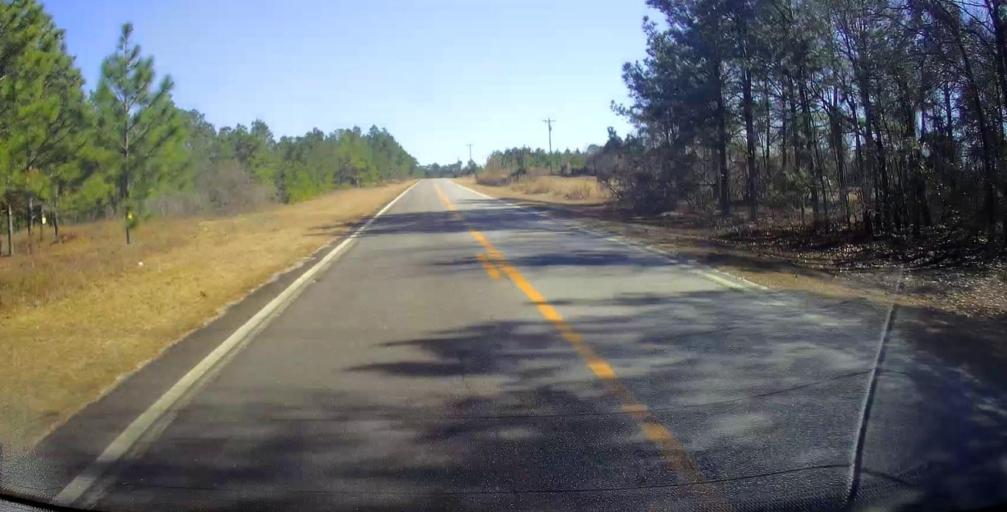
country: US
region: Georgia
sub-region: Crawford County
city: Roberta
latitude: 32.6342
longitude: -83.9951
